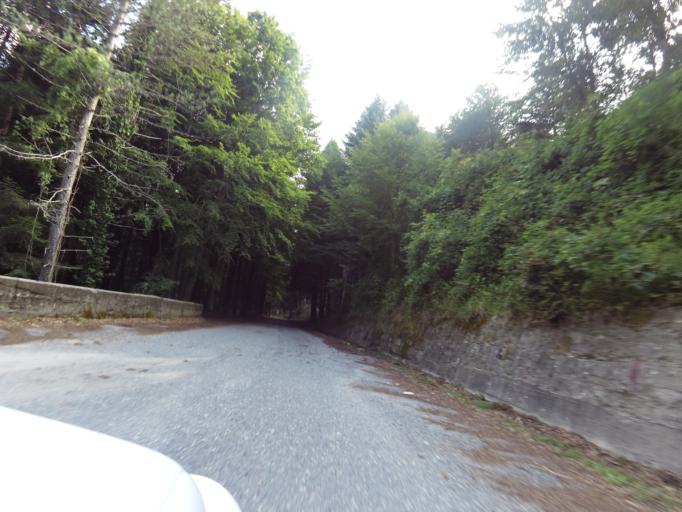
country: IT
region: Calabria
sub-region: Provincia di Vibo-Valentia
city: Nardodipace
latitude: 38.5056
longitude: 16.3765
